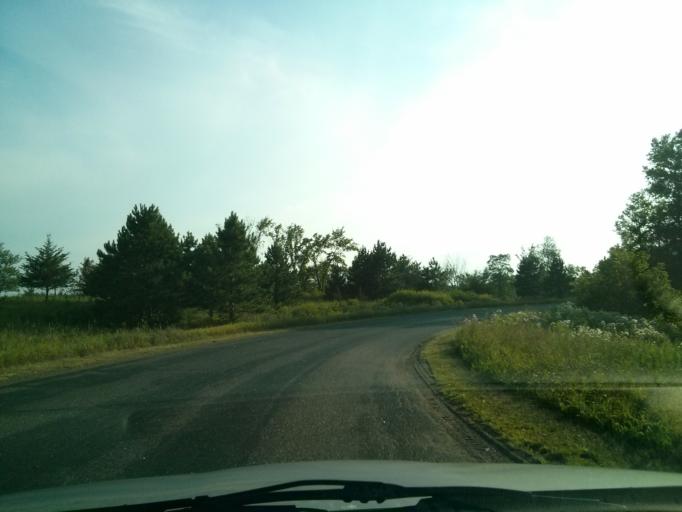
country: US
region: Wisconsin
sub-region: Saint Croix County
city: North Hudson
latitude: 45.0116
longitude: -92.6838
